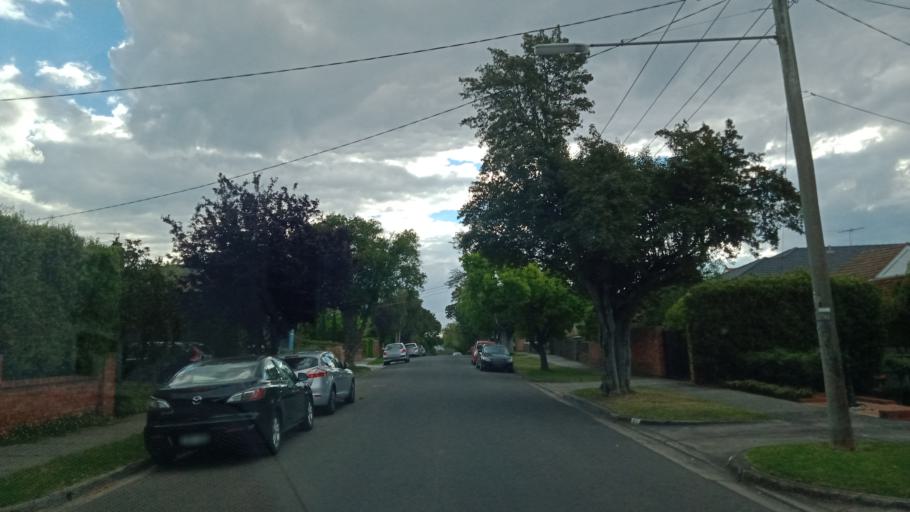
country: AU
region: Victoria
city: Glenferrie
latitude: -37.8364
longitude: 145.0499
